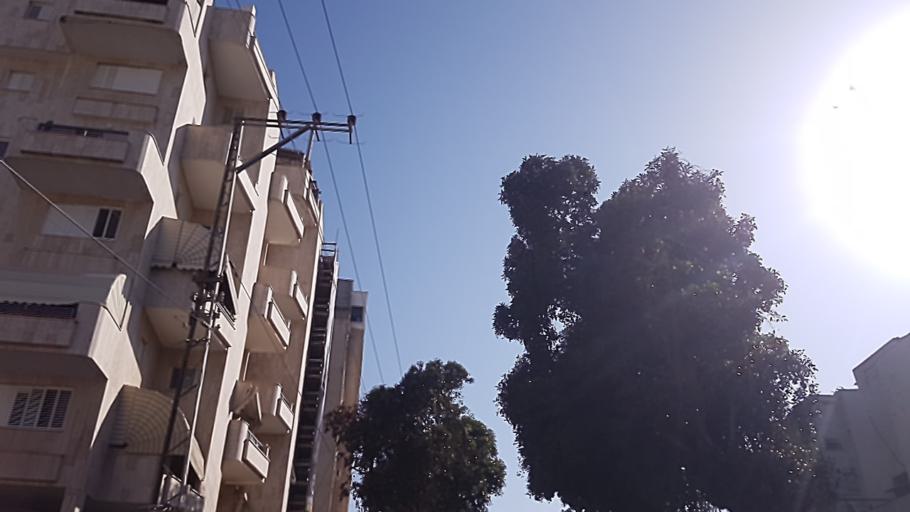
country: IL
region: Tel Aviv
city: Giv`atayim
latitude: 32.0710
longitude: 34.8227
